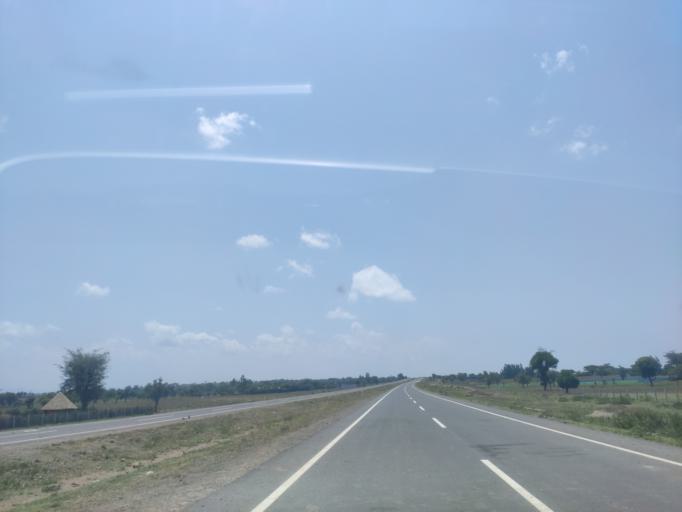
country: ET
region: Oromiya
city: Mojo
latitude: 8.3385
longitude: 38.9698
